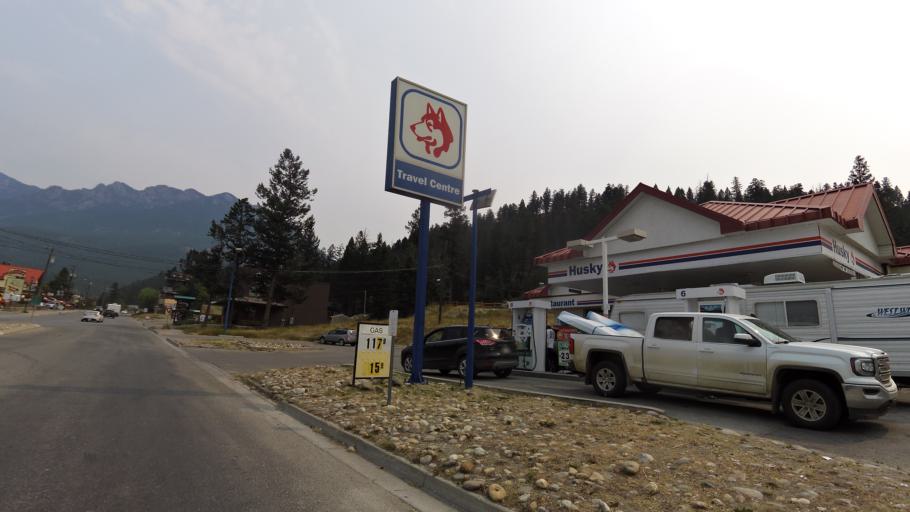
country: CA
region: British Columbia
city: Invermere
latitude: 50.6222
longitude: -116.0712
